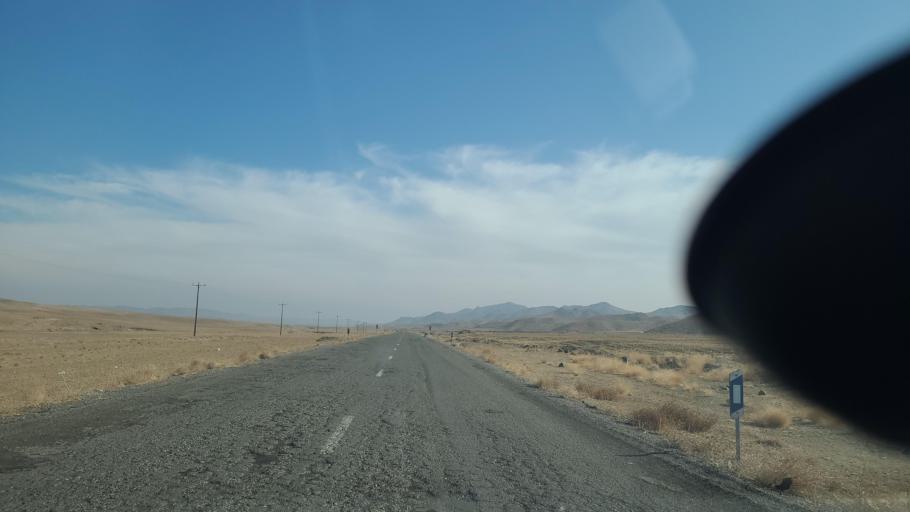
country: IR
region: Razavi Khorasan
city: Fariman
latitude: 35.5891
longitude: 59.6242
